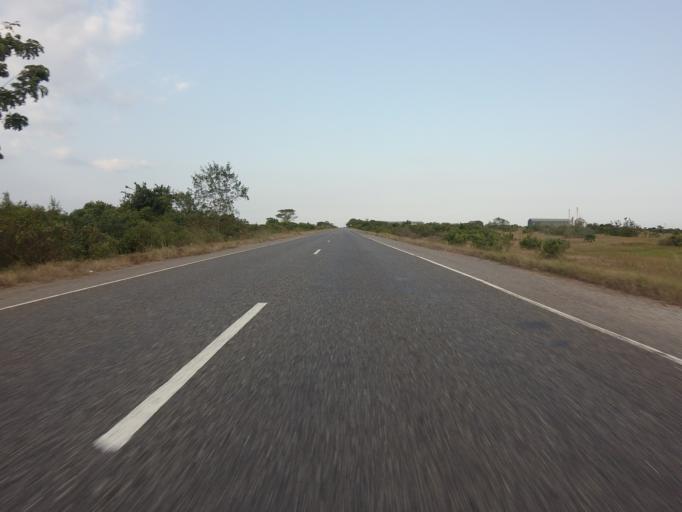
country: GH
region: Volta
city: Anloga
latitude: 6.0815
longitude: 0.5725
